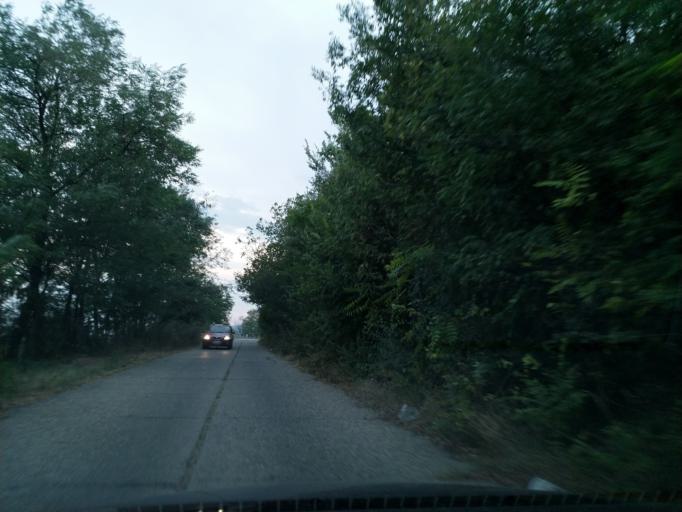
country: RS
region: Central Serbia
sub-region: Pomoravski Okrug
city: Paracin
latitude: 43.8651
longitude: 21.4538
